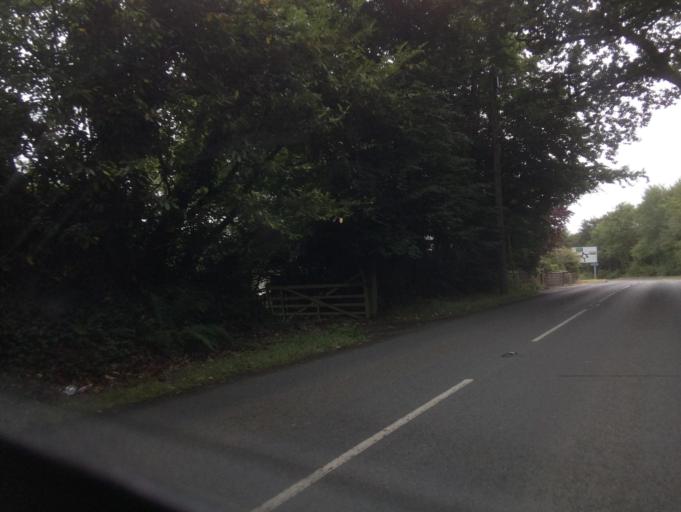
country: GB
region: England
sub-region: Devon
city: Newton Poppleford
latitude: 50.7515
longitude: -3.3292
